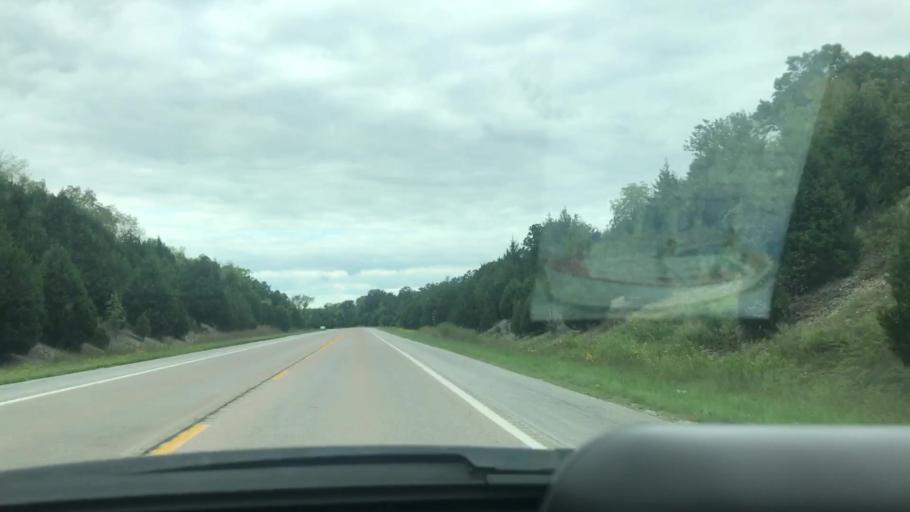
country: US
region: Missouri
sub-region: Benton County
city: Warsaw
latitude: 38.2006
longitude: -93.3257
